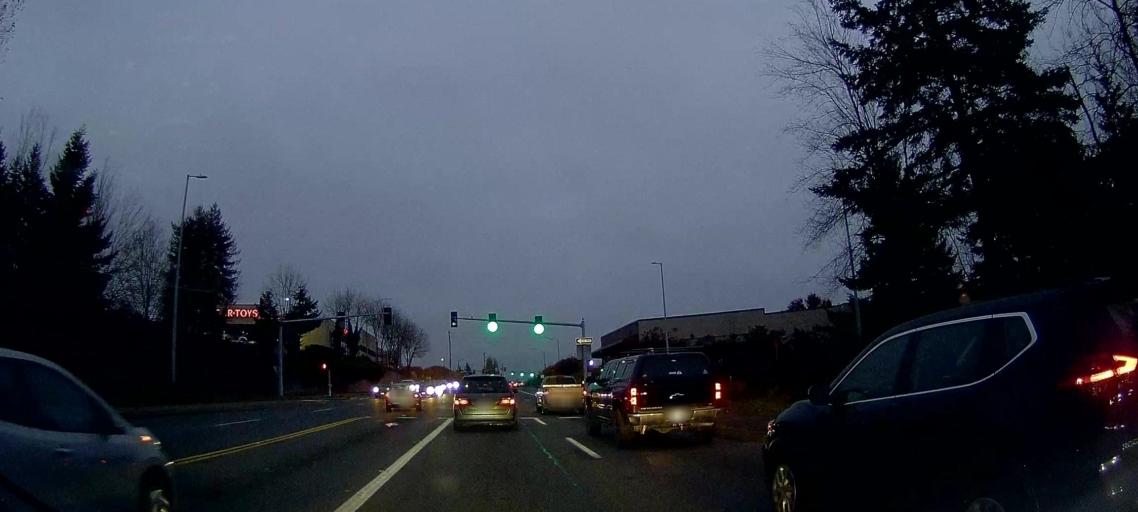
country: US
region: Washington
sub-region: Thurston County
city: Lacey
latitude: 47.0414
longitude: -122.8499
